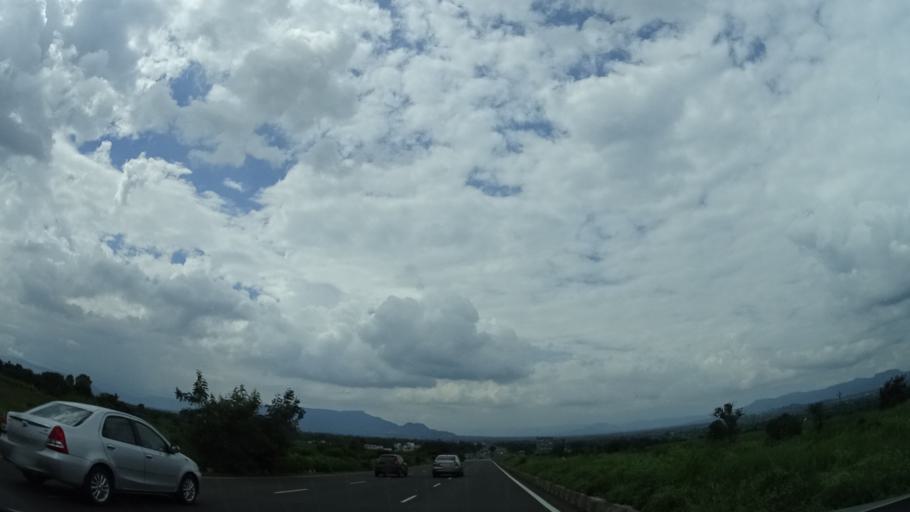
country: IN
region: Maharashtra
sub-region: Satara Division
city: Satara
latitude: 17.7927
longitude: 73.9791
